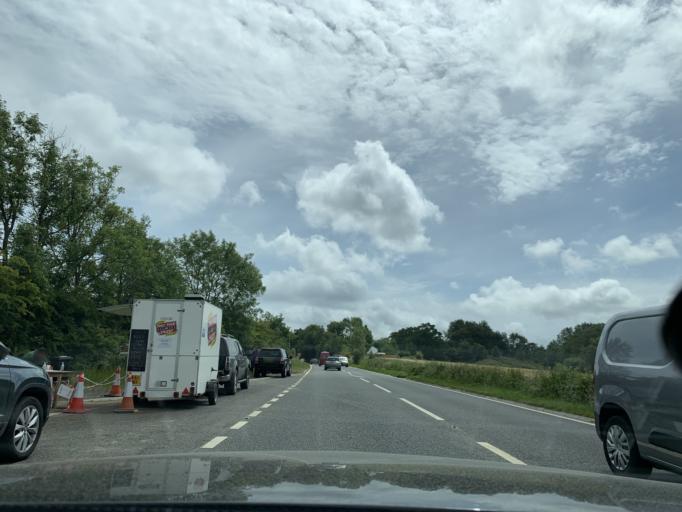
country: GB
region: England
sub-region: East Sussex
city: Robertsbridge
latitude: 50.9670
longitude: 0.4794
